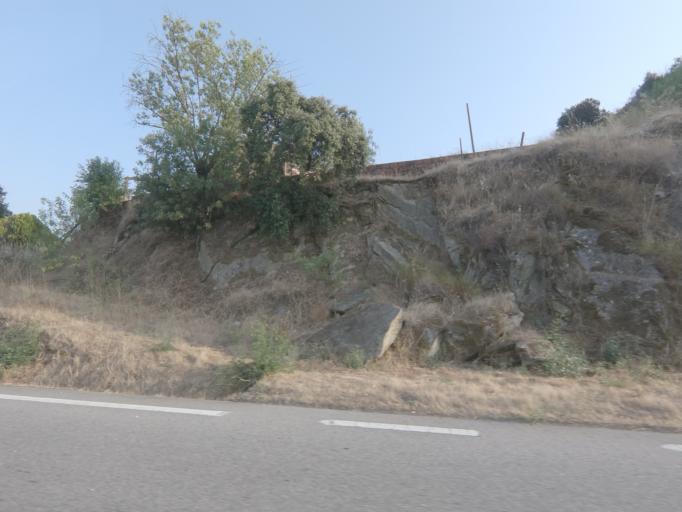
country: PT
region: Viseu
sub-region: Armamar
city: Armamar
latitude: 41.1577
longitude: -7.6428
